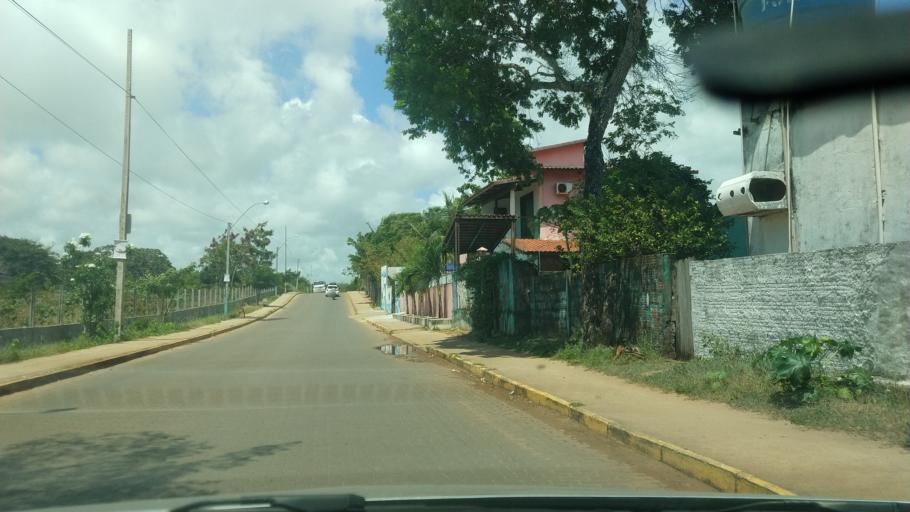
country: BR
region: Rio Grande do Norte
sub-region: Ares
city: Ares
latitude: -6.2339
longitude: -35.0472
